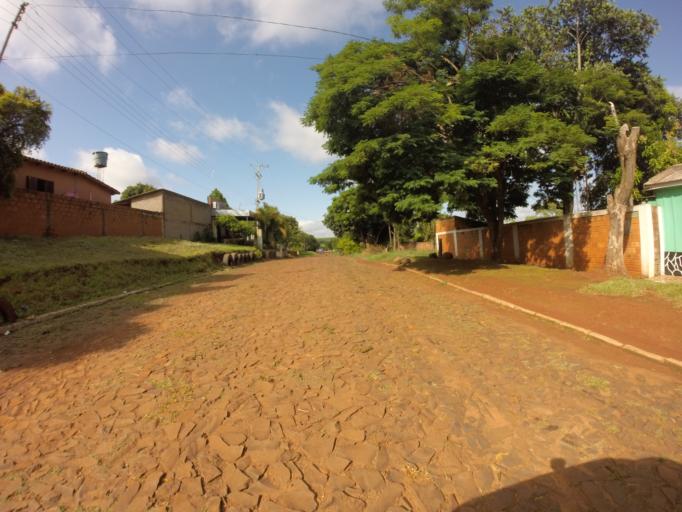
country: PY
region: Alto Parana
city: Ciudad del Este
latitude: -25.4004
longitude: -54.6474
